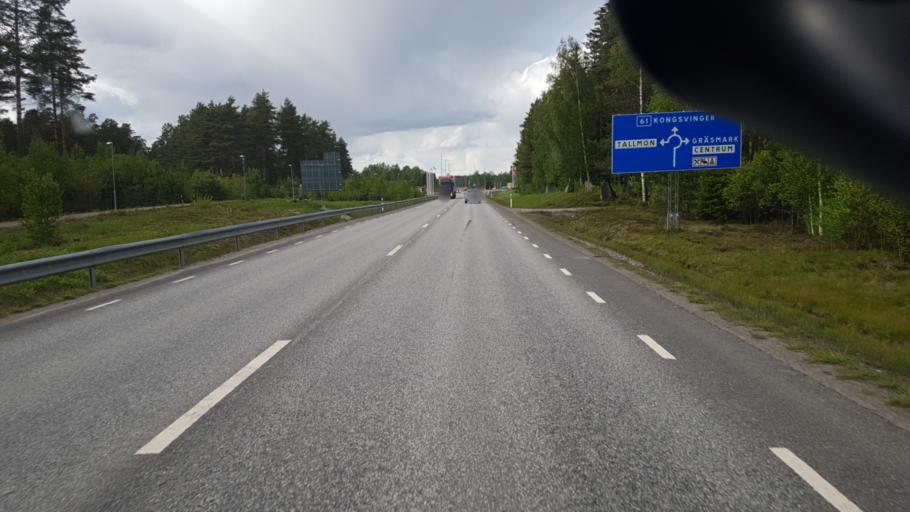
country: SE
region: Vaermland
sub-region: Eda Kommun
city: Charlottenberg
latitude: 59.8754
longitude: 12.2878
